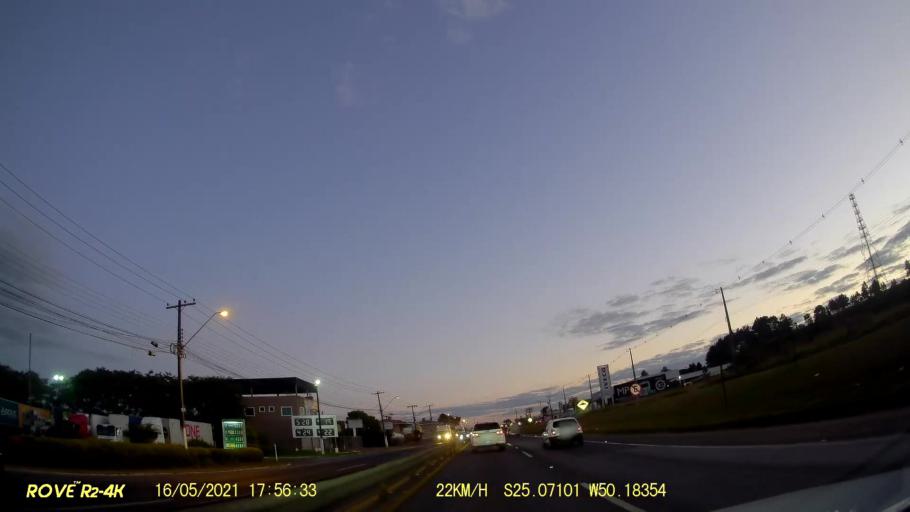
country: BR
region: Parana
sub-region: Ponta Grossa
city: Ponta Grossa
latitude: -25.0709
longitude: -50.1835
